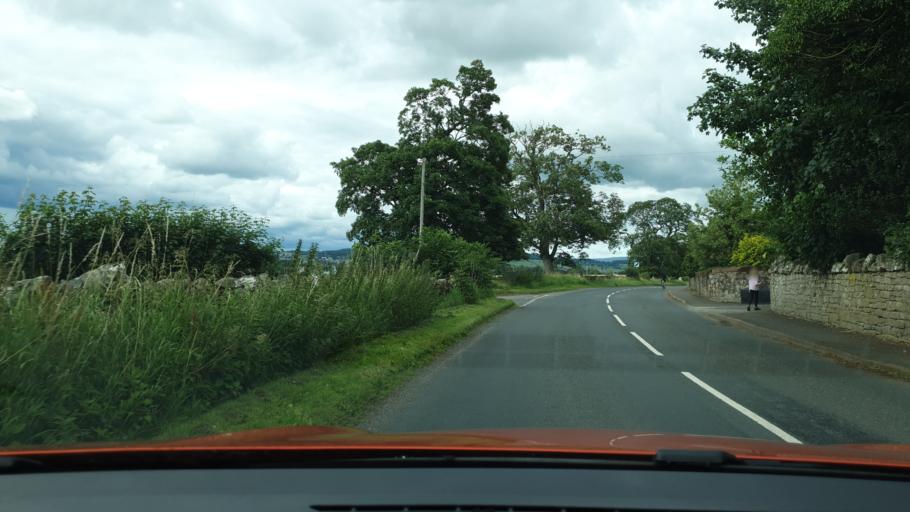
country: GB
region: England
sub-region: Cumbria
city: Penrith
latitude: 54.6340
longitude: -2.7690
